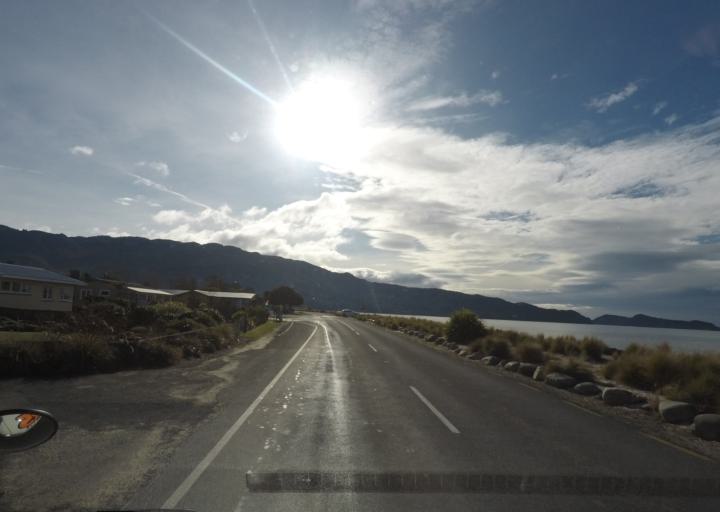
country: NZ
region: Tasman
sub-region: Tasman District
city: Motueka
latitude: -41.0061
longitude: 173.0097
